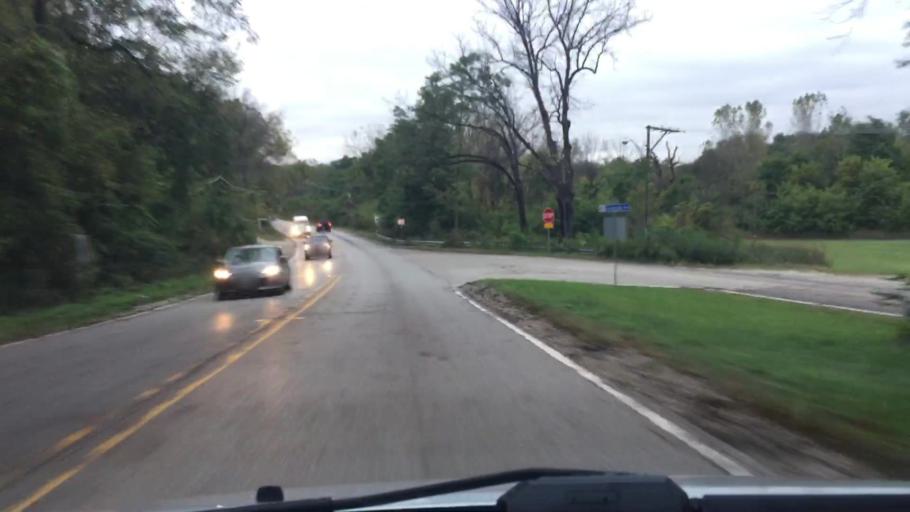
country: US
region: Illinois
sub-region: Kane County
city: Sleepy Hollow
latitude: 42.1164
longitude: -88.2969
